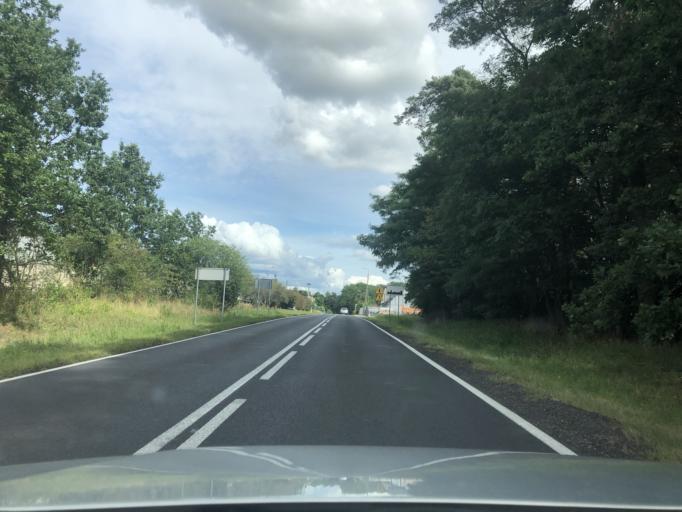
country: PL
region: Greater Poland Voivodeship
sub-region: Powiat pilski
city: Szydlowo
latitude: 53.0769
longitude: 16.5946
